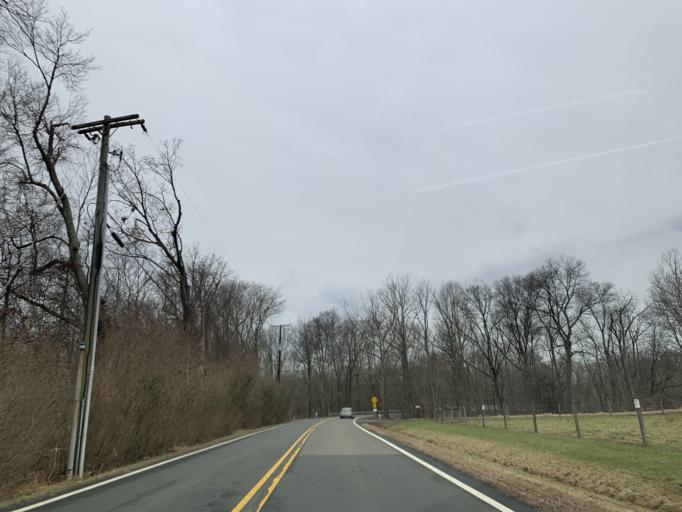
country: US
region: New Jersey
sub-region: Somerset County
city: Bridgewater
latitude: 40.6357
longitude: -74.6794
